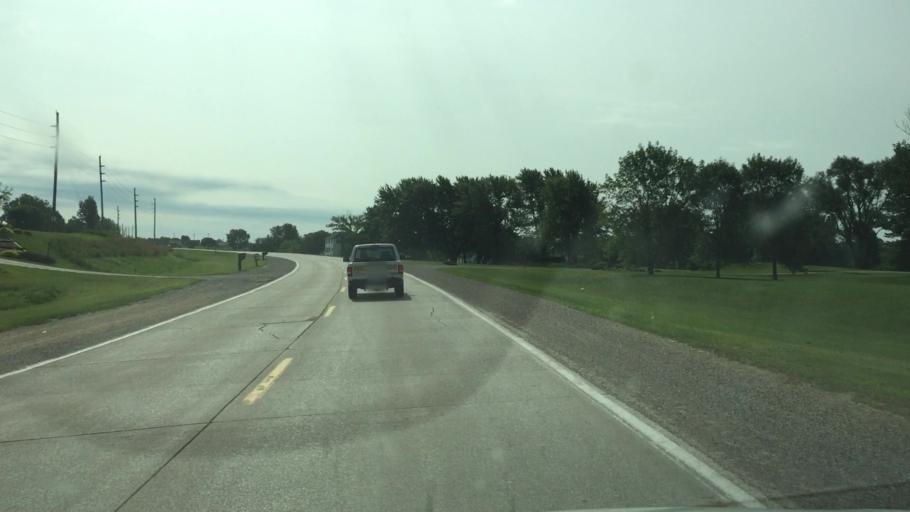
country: US
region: Illinois
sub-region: Hancock County
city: Nauvoo
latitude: 40.6322
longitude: -91.5118
